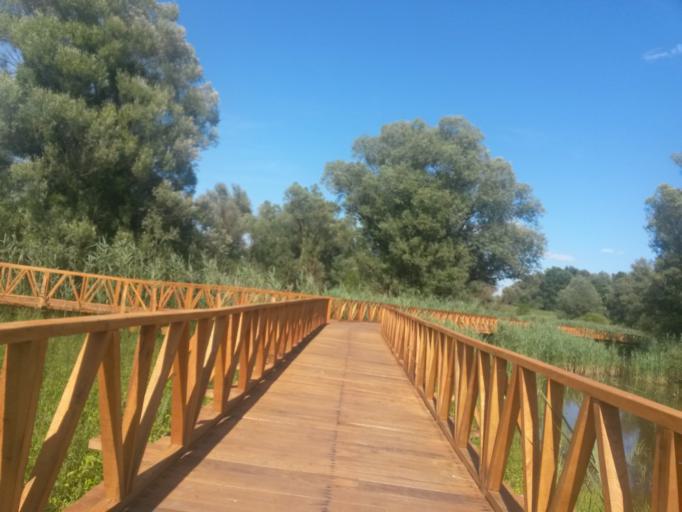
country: HR
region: Osjecko-Baranjska
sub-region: Grad Osijek
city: Bilje
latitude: 45.6081
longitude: 18.7956
